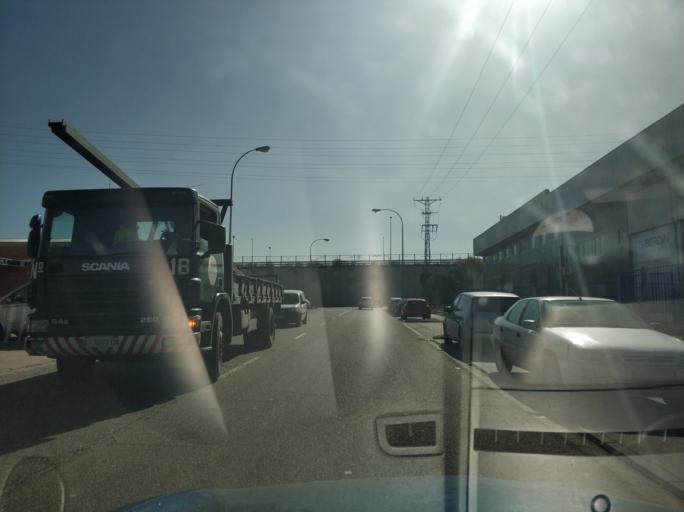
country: ES
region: Castille and Leon
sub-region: Provincia de Valladolid
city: Cisterniga
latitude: 41.6210
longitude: -4.6971
